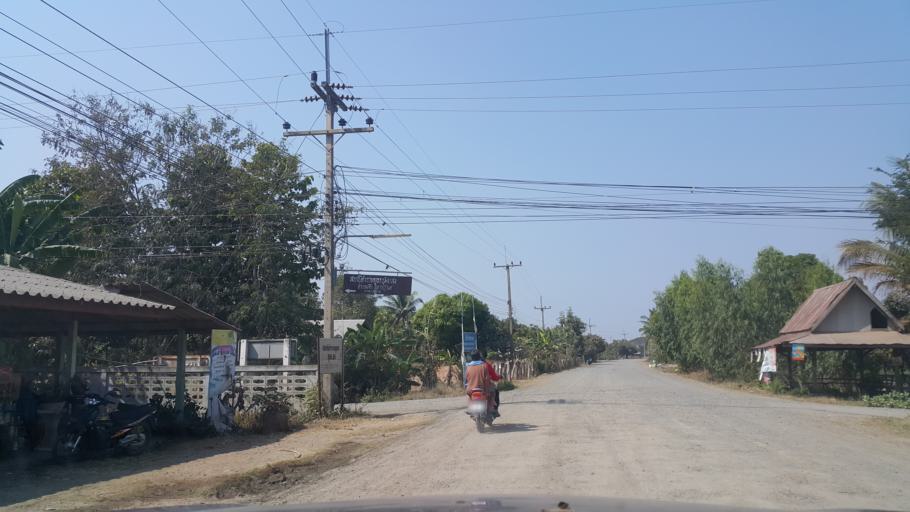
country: TH
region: Buriram
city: Satuek
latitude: 15.1324
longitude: 103.3477
